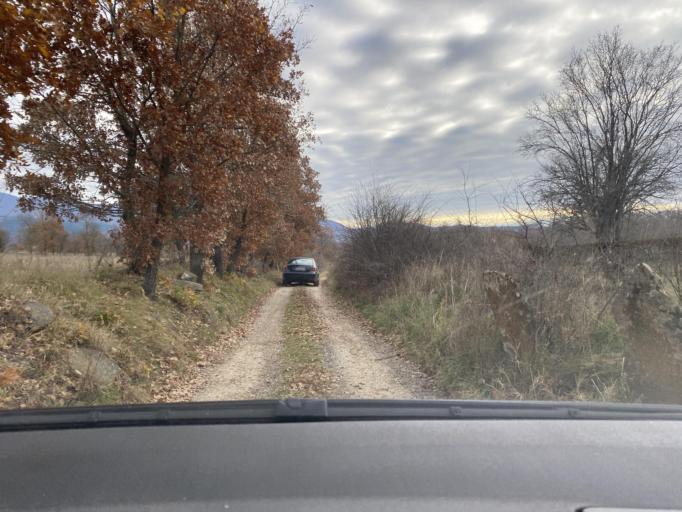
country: MK
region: Opstina Rankovce
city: Rankovce
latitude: 42.1830
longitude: 22.1251
